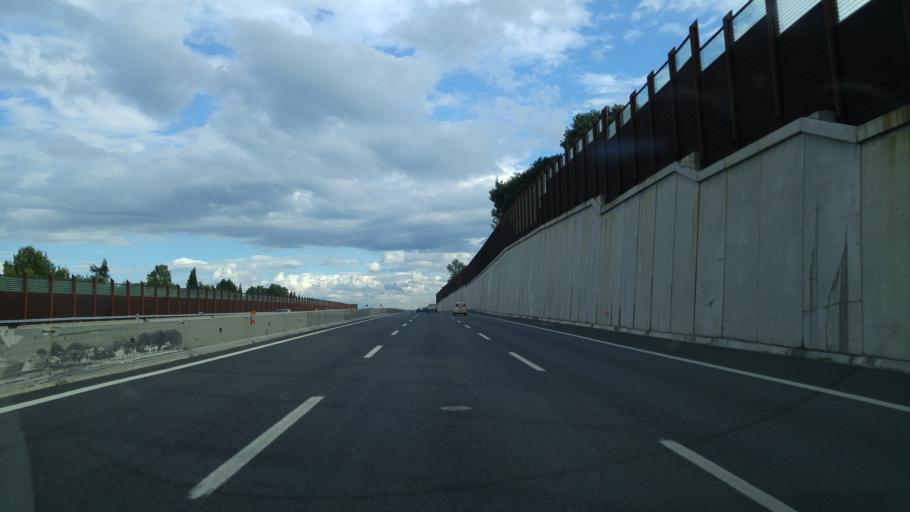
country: IT
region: Emilia-Romagna
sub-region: Provincia di Rimini
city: Rivazzurra
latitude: 44.0219
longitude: 12.5835
